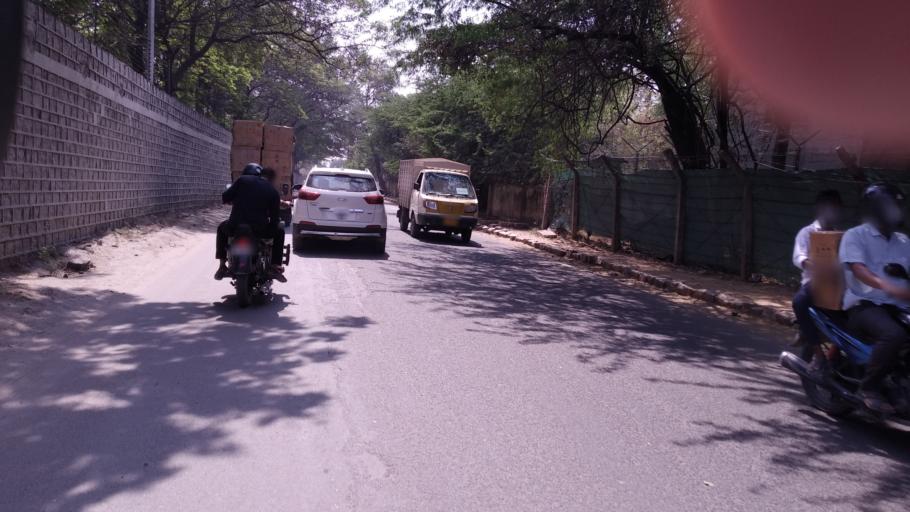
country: IN
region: Telangana
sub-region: Hyderabad
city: Malkajgiri
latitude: 17.4619
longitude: 78.4848
